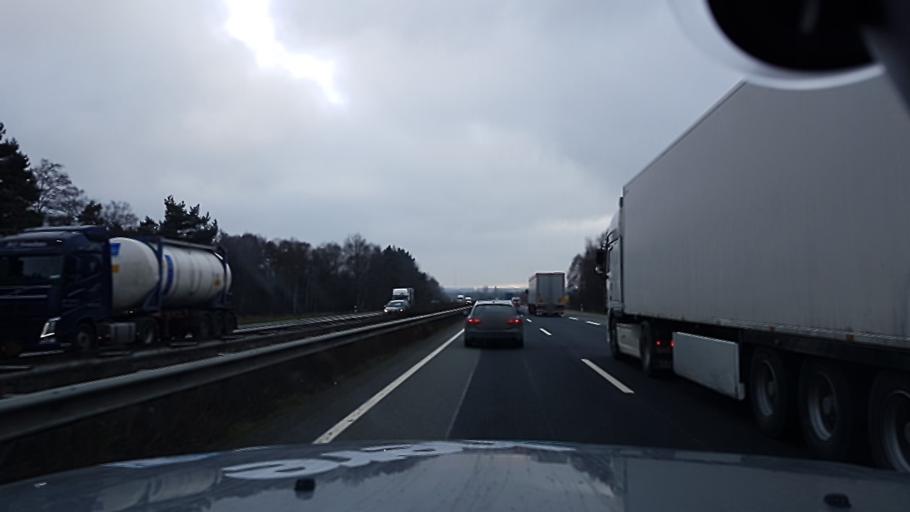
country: DE
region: Lower Saxony
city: Rieste
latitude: 52.4266
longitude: 8.0314
